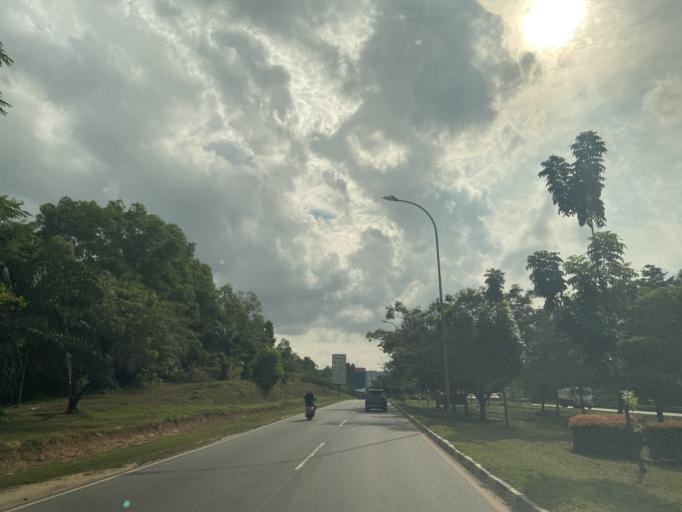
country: SG
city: Singapore
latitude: 1.0986
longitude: 104.0522
